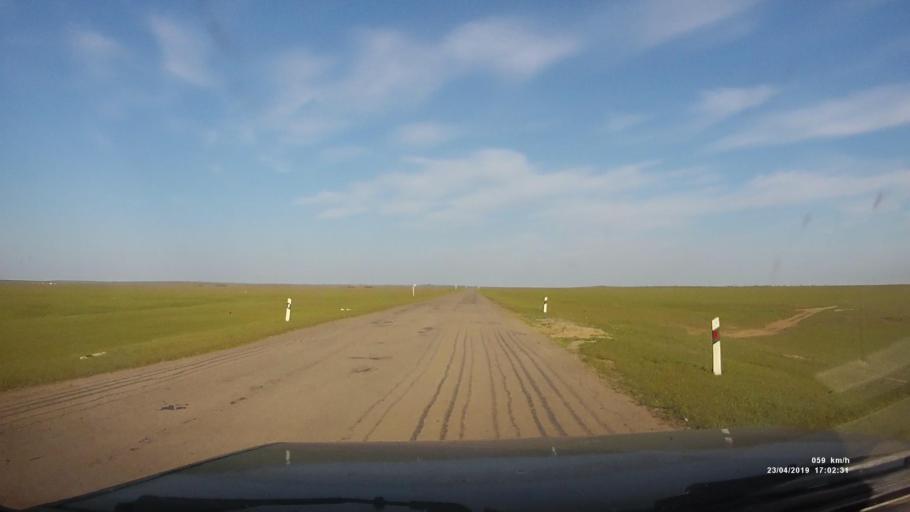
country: RU
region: Kalmykiya
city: Priyutnoye
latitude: 46.2924
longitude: 43.4187
